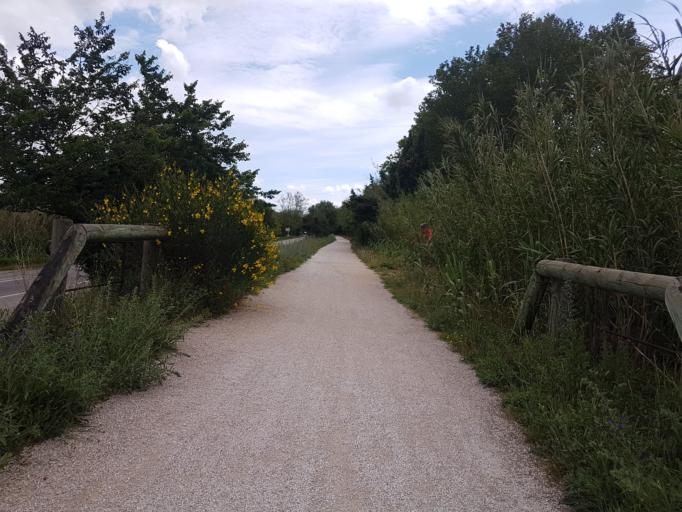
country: FR
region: Languedoc-Roussillon
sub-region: Departement du Gard
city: Beaucaire
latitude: 43.8250
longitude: 4.6268
